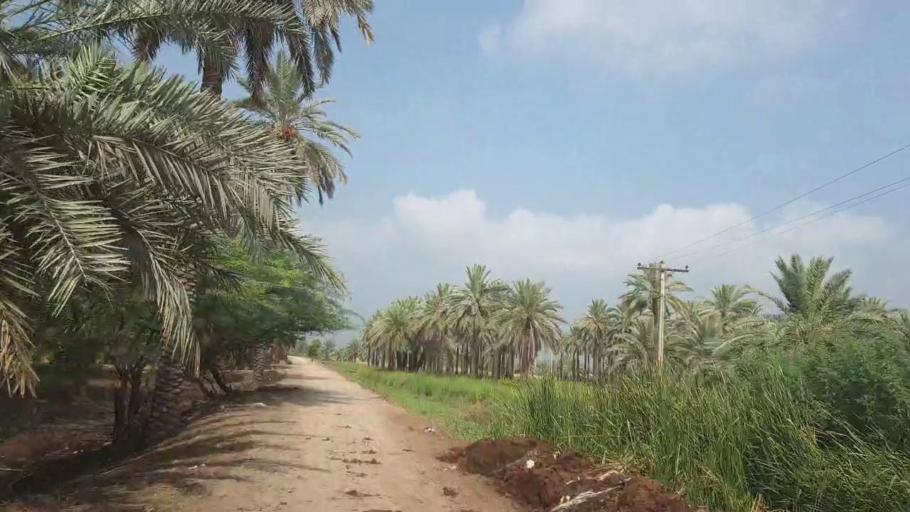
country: PK
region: Sindh
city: Khairpur
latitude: 27.5615
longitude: 68.7624
